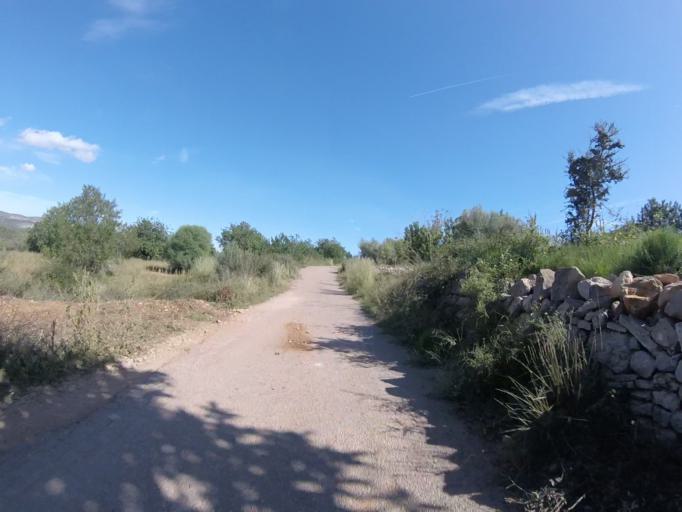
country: ES
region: Valencia
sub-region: Provincia de Castello
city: Santa Magdalena de Pulpis
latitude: 40.3601
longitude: 0.3129
